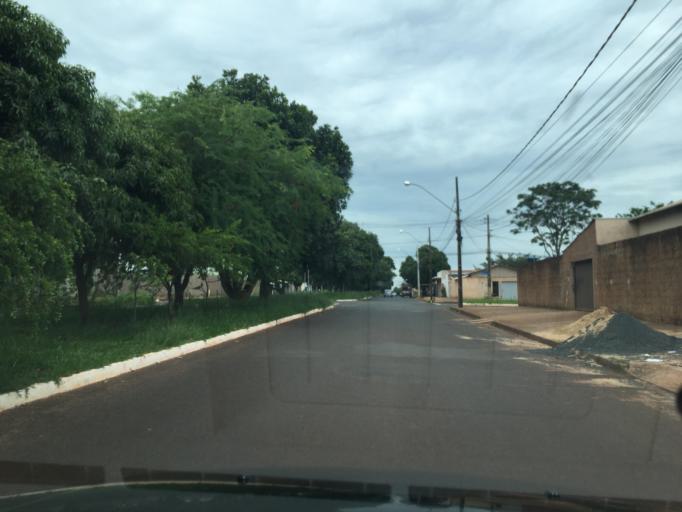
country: BR
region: Minas Gerais
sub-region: Uberlandia
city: Uberlandia
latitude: -18.8740
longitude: -48.2260
